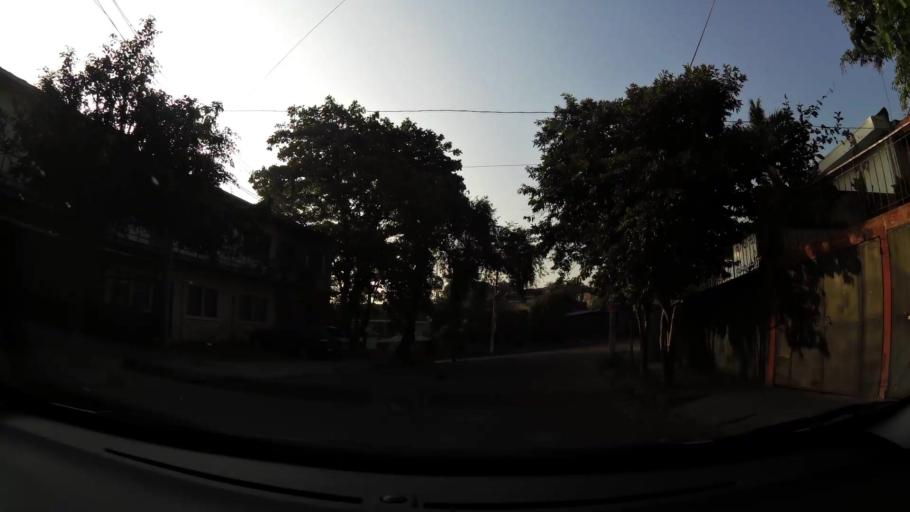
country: SV
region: San Salvador
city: San Salvador
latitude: 13.6864
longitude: -89.1970
